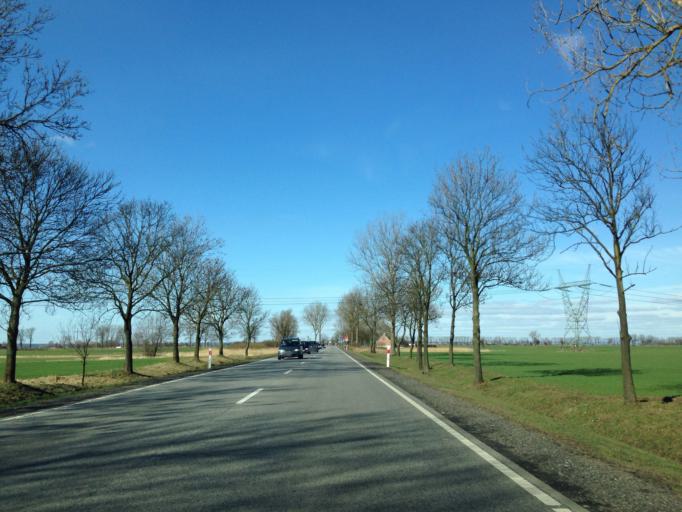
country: PL
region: Pomeranian Voivodeship
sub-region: Powiat malborski
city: Miloradz
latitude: 54.0486
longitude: 18.9507
